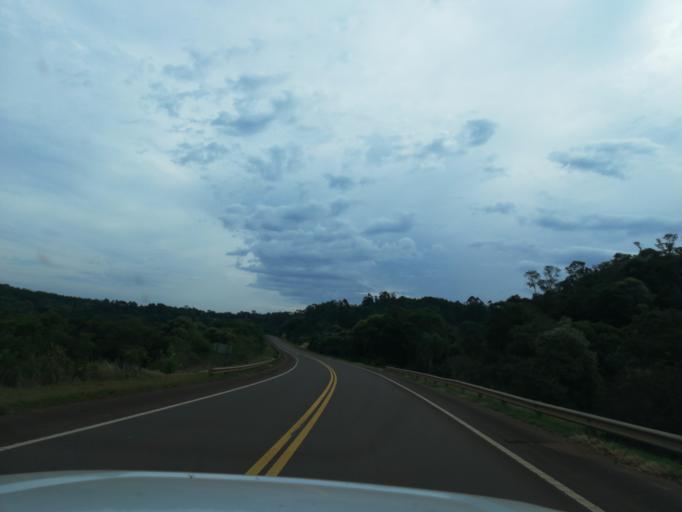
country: AR
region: Misiones
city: San Vicente
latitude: -26.7129
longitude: -54.2361
